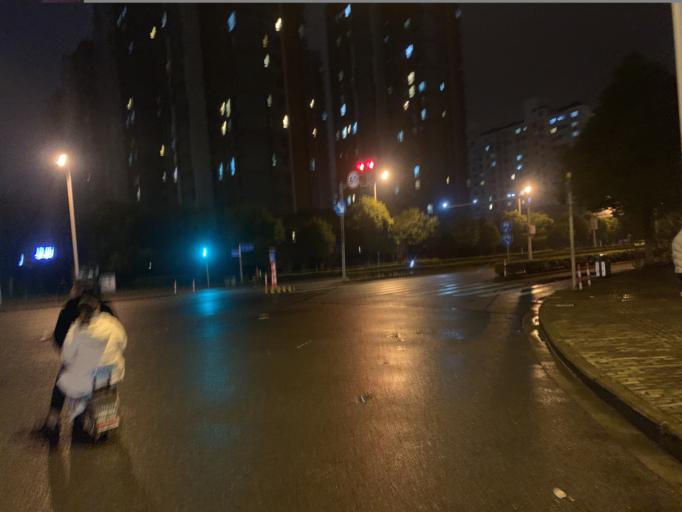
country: CN
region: Shanghai Shi
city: Huamu
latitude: 31.2052
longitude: 121.6303
